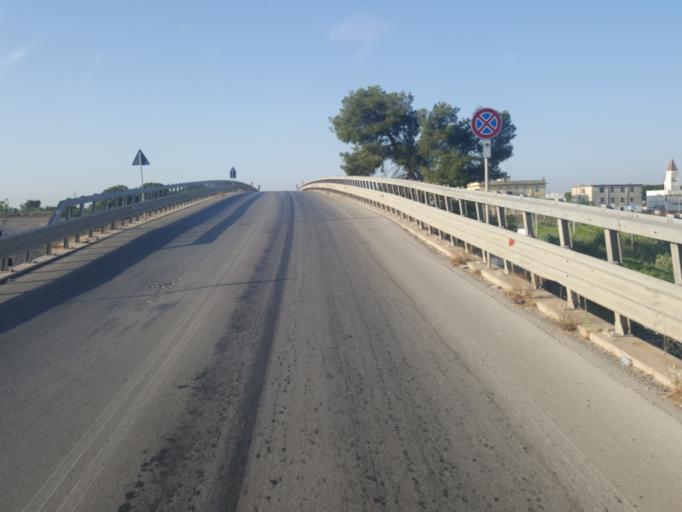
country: IT
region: Apulia
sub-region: Provincia di Foggia
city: Cerignola
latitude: 41.3176
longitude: 15.9000
